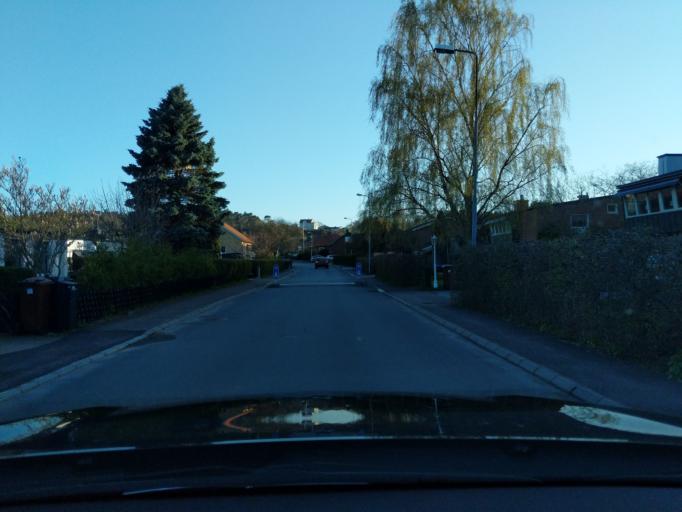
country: SE
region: Vaestra Goetaland
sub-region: Goteborg
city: Majorna
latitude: 57.6377
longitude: 11.9303
